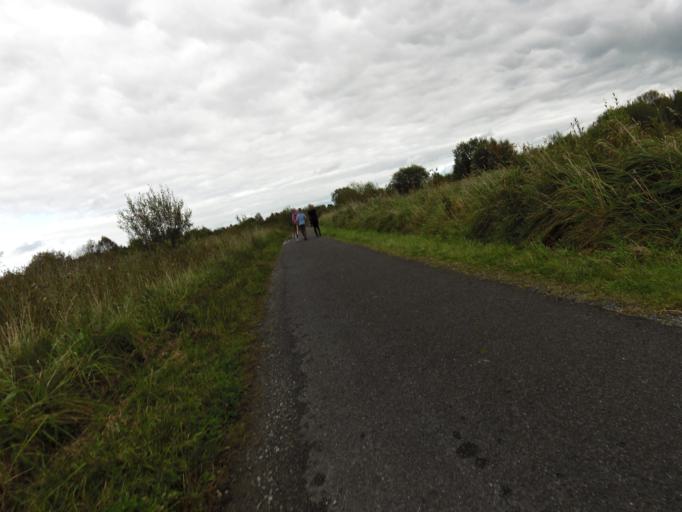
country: IE
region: Leinster
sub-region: Uibh Fhaili
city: Ferbane
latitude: 53.2224
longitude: -7.7374
